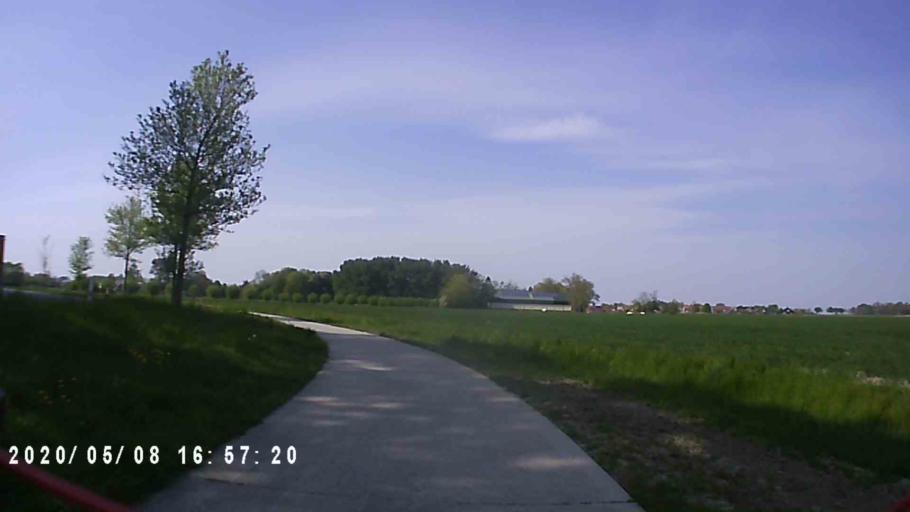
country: NL
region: Groningen
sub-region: Gemeente Bedum
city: Bedum
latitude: 53.3960
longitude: 6.6150
